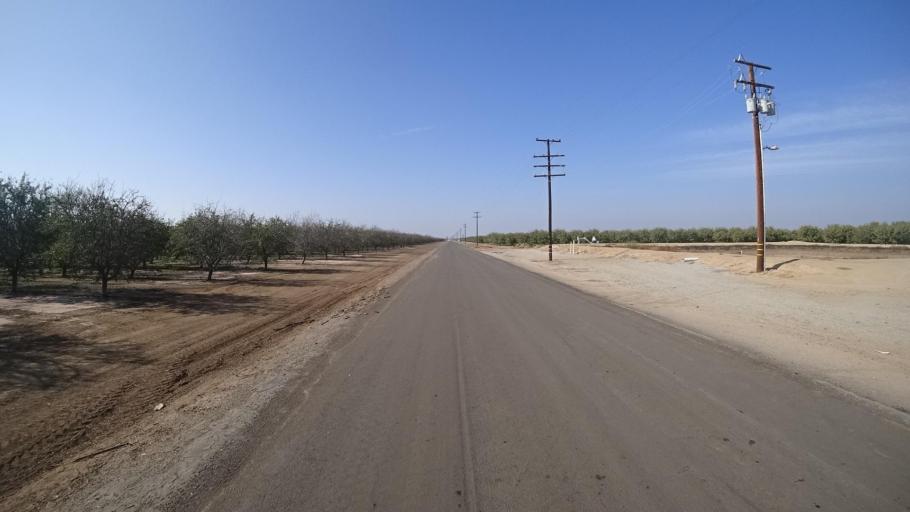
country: US
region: California
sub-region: Kern County
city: McFarland
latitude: 35.6601
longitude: -119.1817
